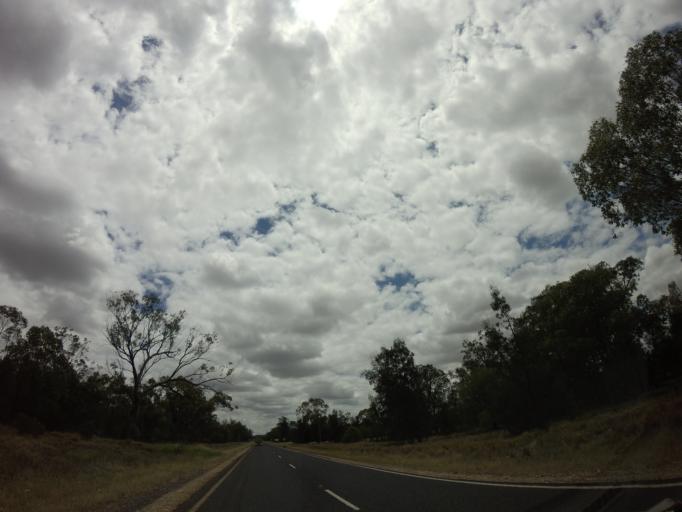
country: AU
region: Queensland
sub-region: Goondiwindi
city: Goondiwindi
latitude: -28.4529
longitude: 150.2980
